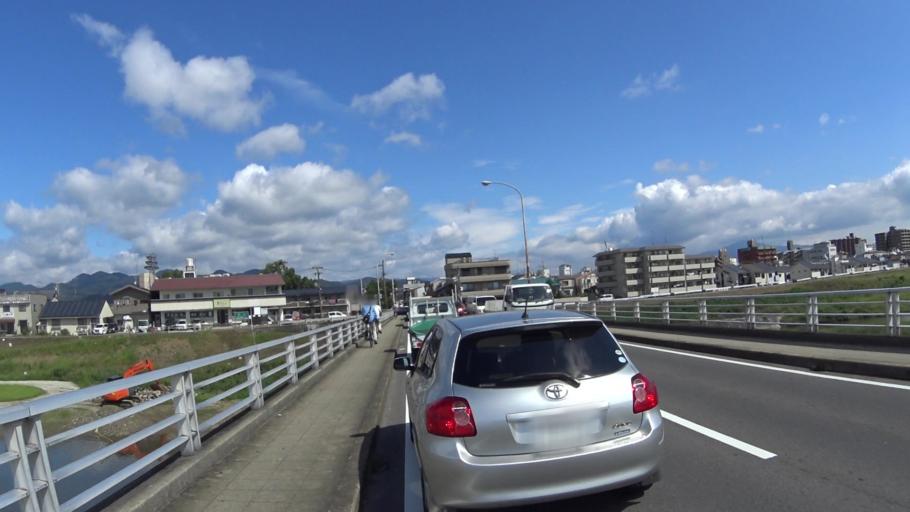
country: JP
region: Kyoto
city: Muko
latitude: 34.9991
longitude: 135.7046
